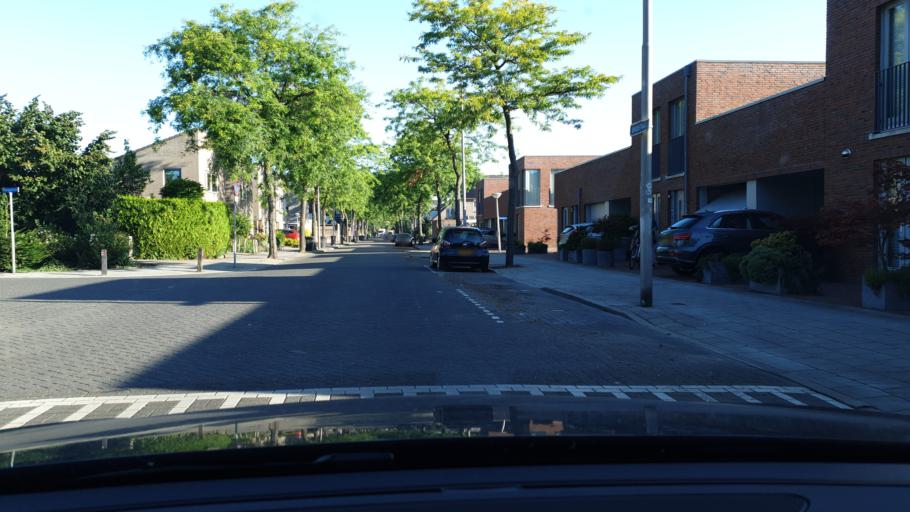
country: NL
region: North Brabant
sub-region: Gemeente Eindhoven
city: Eindhoven
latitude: 51.4417
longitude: 5.4524
